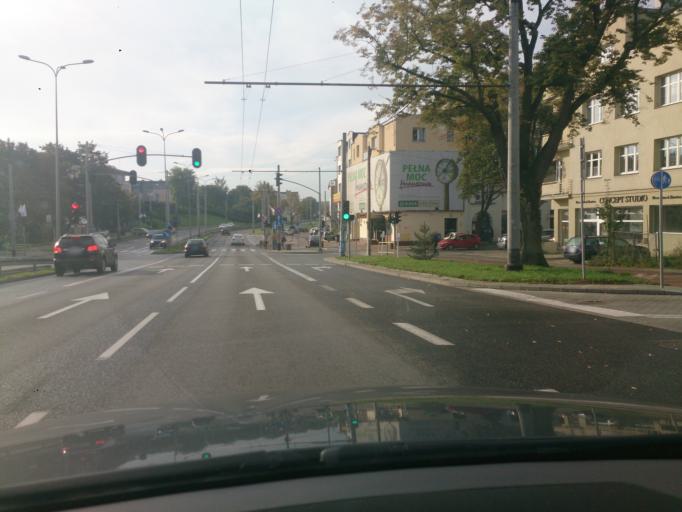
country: PL
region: Pomeranian Voivodeship
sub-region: Sopot
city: Sopot
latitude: 54.4797
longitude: 18.5522
